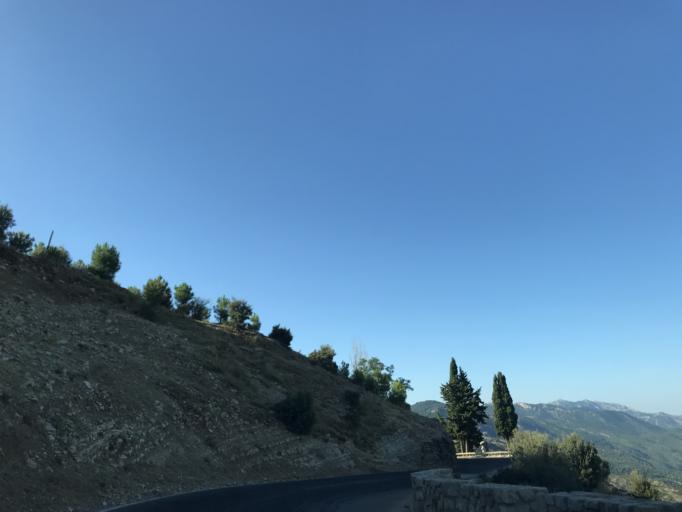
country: ES
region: Andalusia
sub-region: Provincia de Jaen
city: La Iruela
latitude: 37.9422
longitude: -2.9398
